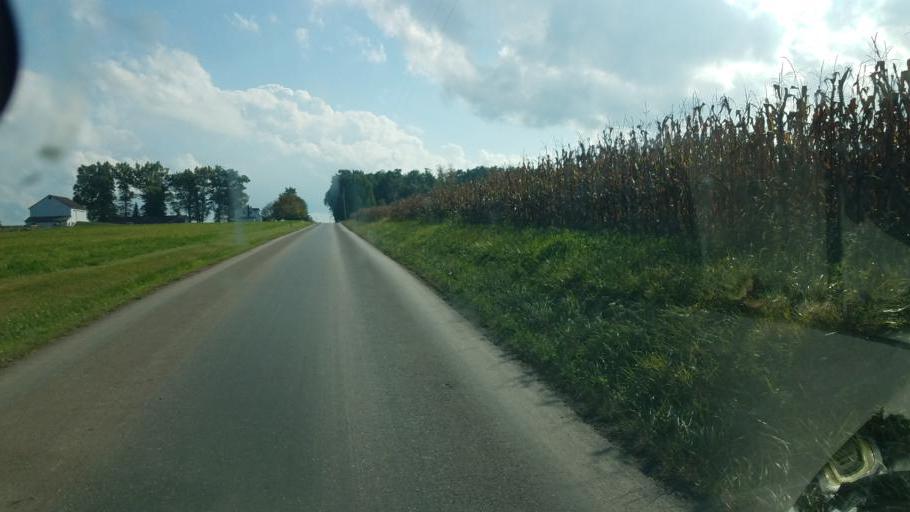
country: US
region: Ohio
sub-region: Wayne County
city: Apple Creek
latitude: 40.6631
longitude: -81.8419
